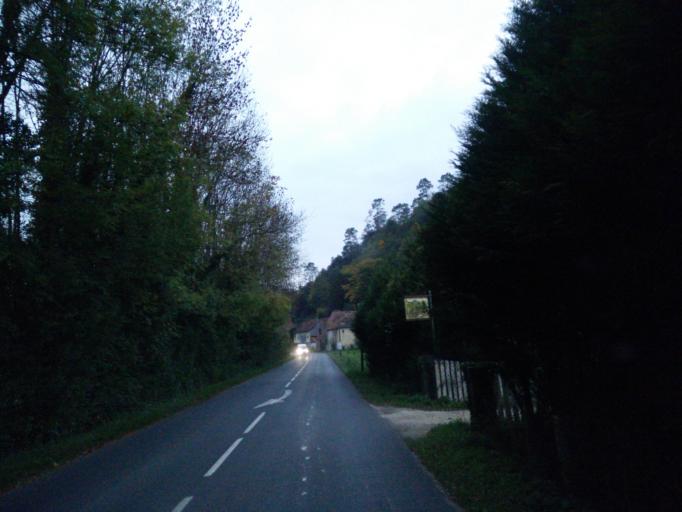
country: FR
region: Aquitaine
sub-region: Departement de la Dordogne
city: Carsac-Aillac
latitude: 44.8480
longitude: 1.2725
